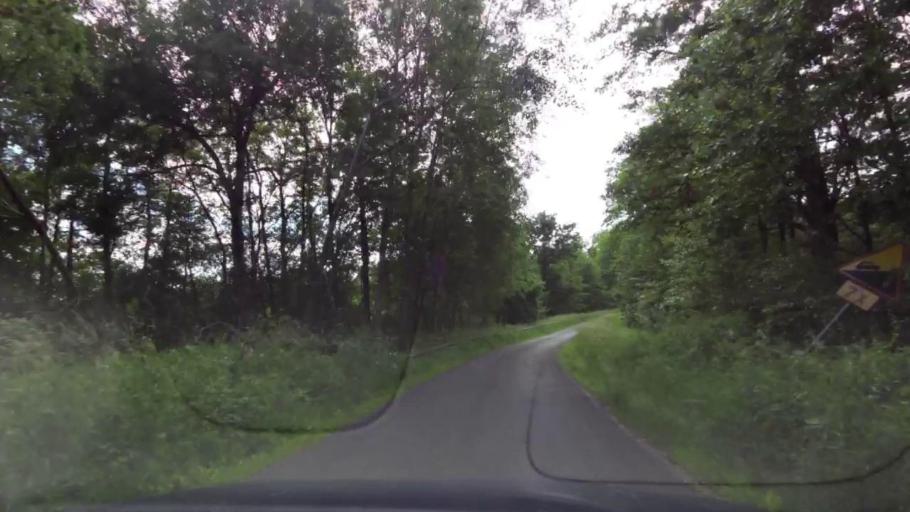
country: PL
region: West Pomeranian Voivodeship
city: Trzcinsko Zdroj
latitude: 52.8846
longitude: 14.5995
